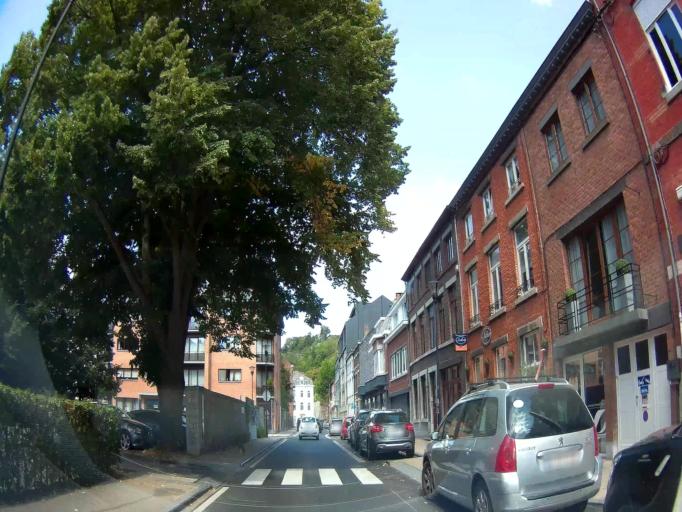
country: BE
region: Wallonia
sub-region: Province de Namur
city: Dinant
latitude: 50.2535
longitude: 4.9173
